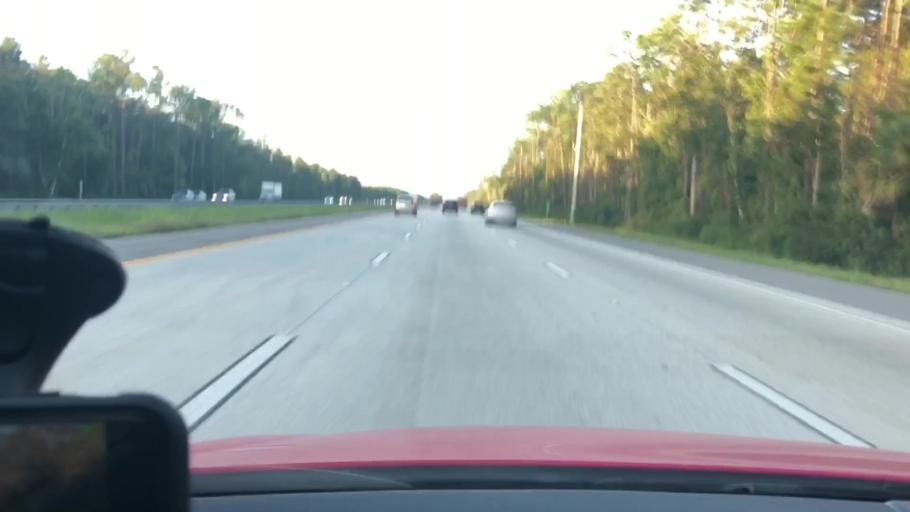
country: US
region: Florida
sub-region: Volusia County
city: Lake Helen
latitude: 29.0474
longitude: -81.2038
